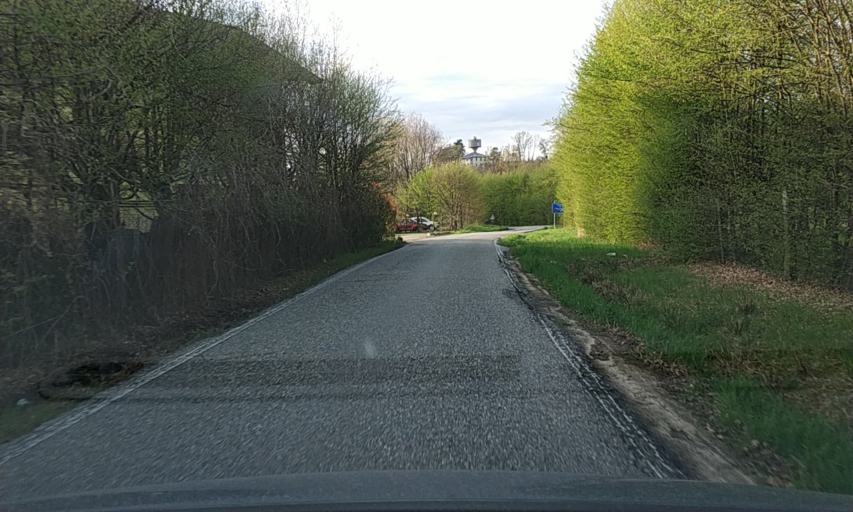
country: IT
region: Piedmont
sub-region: Provincia di Torino
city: Fiano
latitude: 45.2160
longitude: 7.5476
